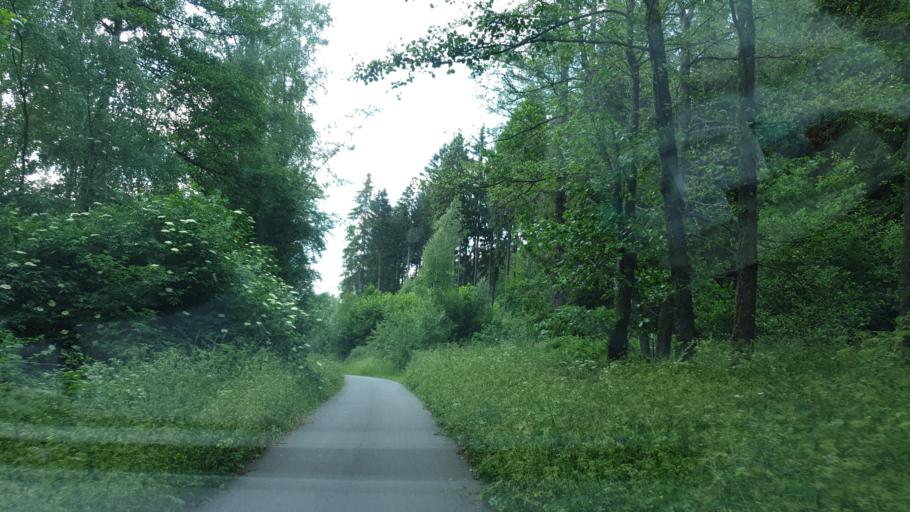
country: DE
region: Saxony
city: Adorf
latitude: 50.3386
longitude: 12.2543
